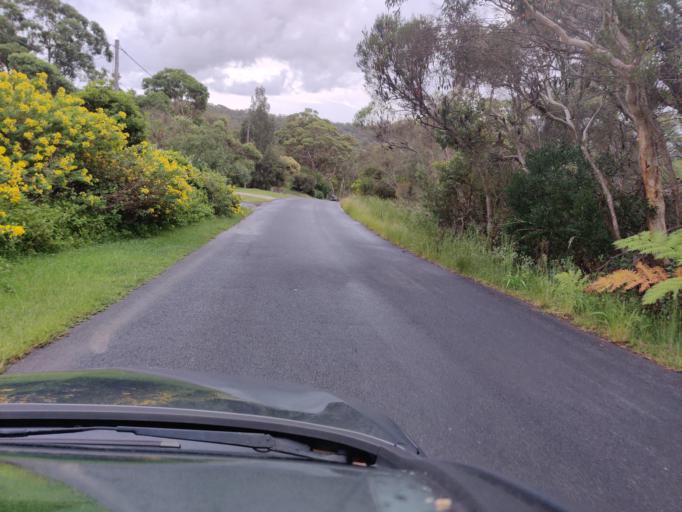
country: AU
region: New South Wales
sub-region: Pittwater
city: Ingleside
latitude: -33.6782
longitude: 151.2536
